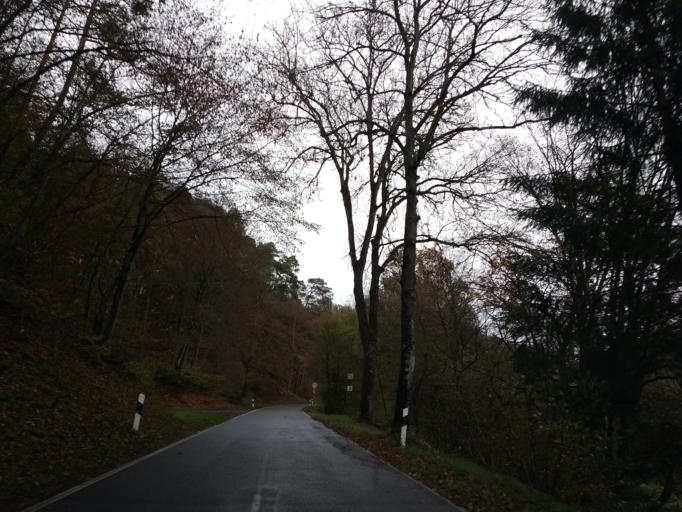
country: DE
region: Hesse
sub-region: Regierungsbezirk Kassel
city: Vohl
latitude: 51.1910
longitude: 8.9493
